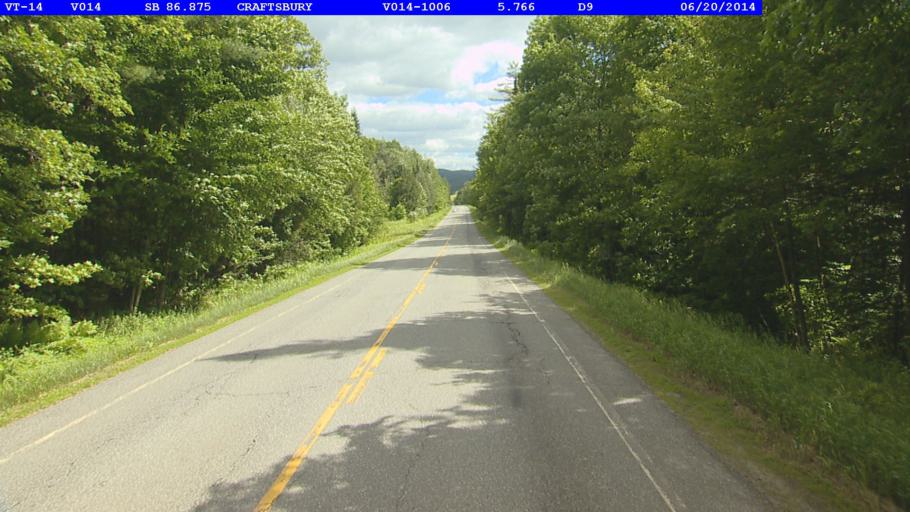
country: US
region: Vermont
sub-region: Caledonia County
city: Hardwick
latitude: 44.6735
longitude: -72.4048
